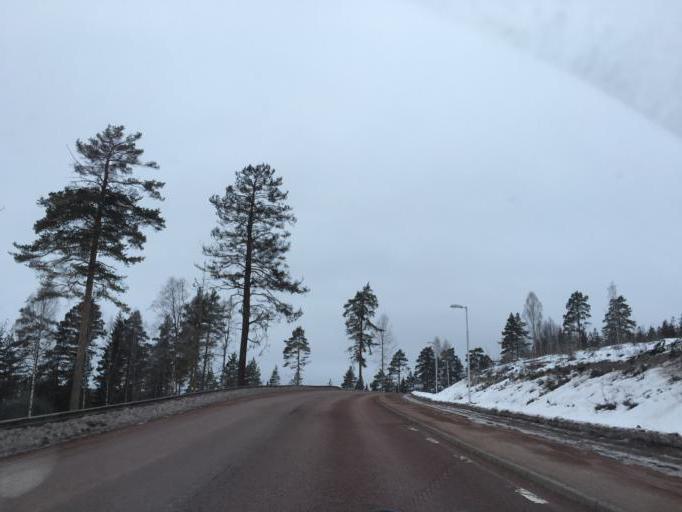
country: SE
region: Dalarna
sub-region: Alvdalens Kommun
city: AElvdalen
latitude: 61.2417
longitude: 14.0327
